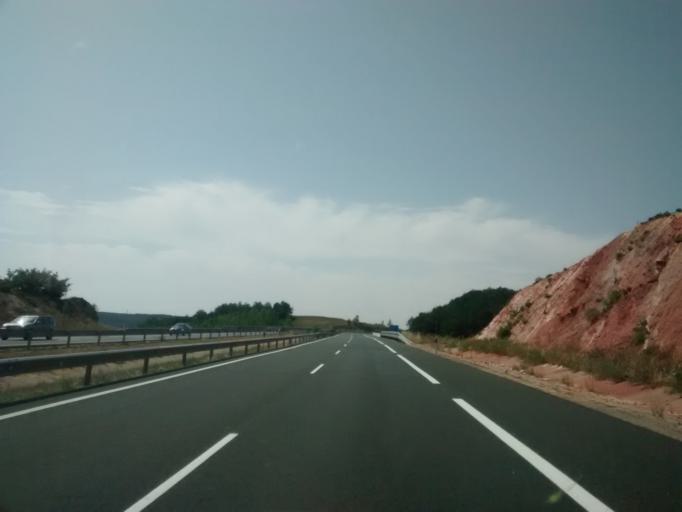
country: ES
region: Castille and Leon
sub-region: Provincia de Palencia
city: Aguilar de Campoo
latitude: 42.7336
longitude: -4.2887
